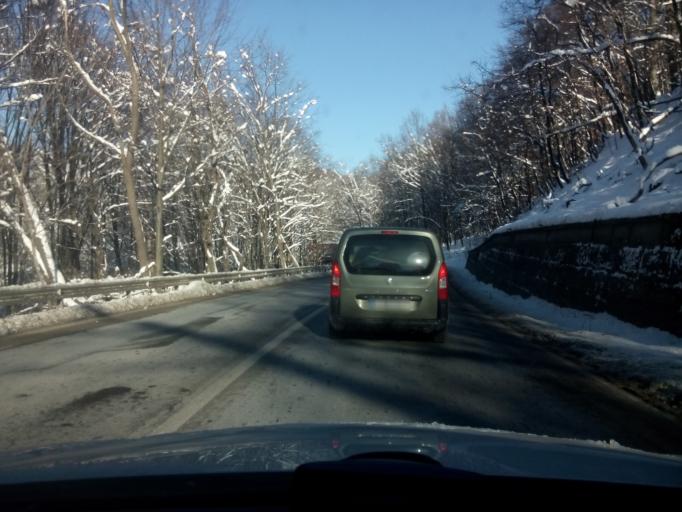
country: RO
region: Arges
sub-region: Comuna Cotmeana
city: Cotmeana
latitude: 44.9999
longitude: 24.6055
